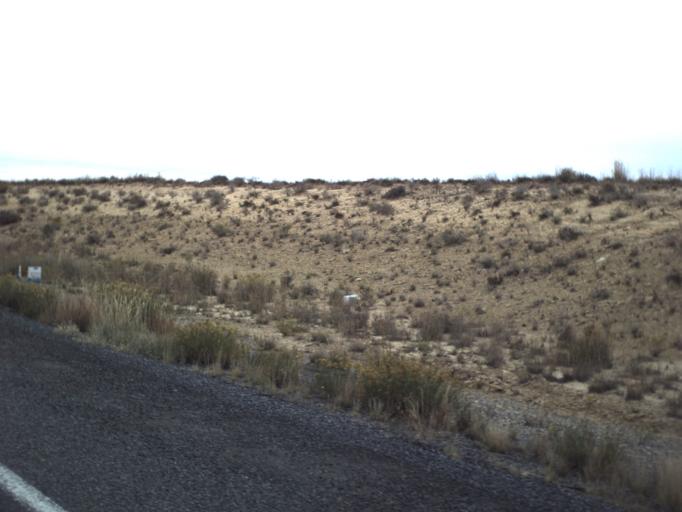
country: US
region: Utah
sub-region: Emery County
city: Castle Dale
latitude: 38.8814
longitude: -110.6570
